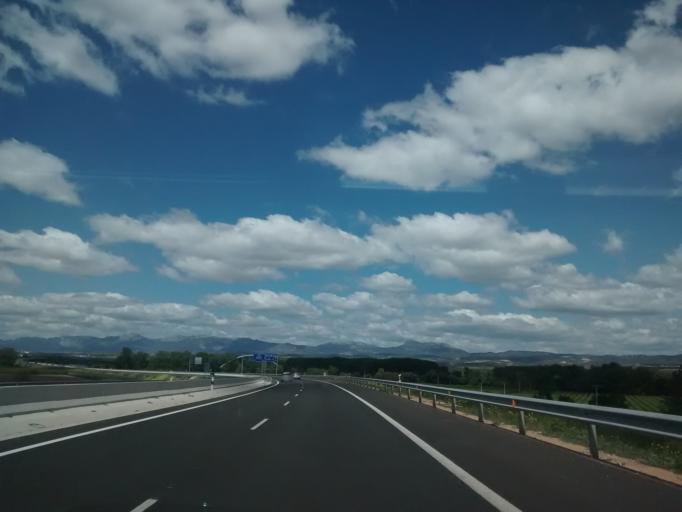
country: ES
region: Navarre
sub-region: Provincia de Navarra
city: Viana
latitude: 42.4547
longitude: -2.3598
